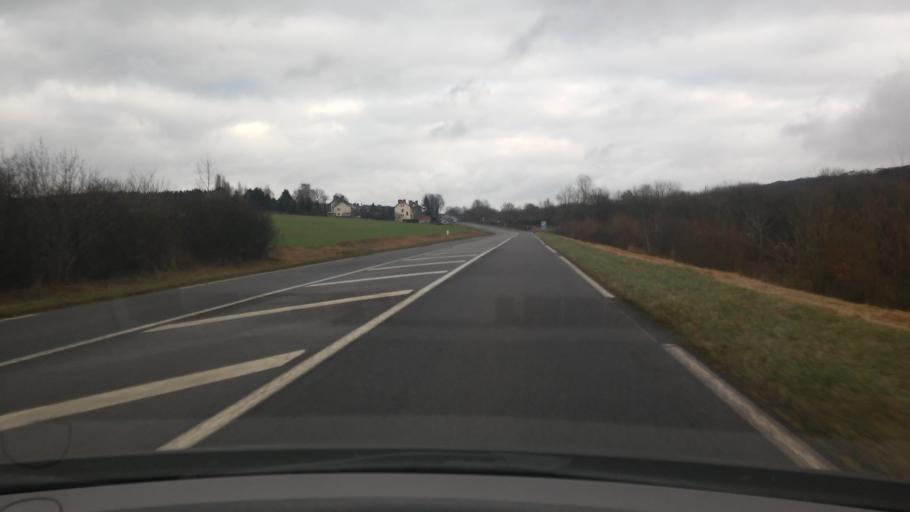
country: FR
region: Lorraine
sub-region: Departement de la Moselle
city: Longeville-les-Saint-Avold
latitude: 49.1190
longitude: 6.5764
